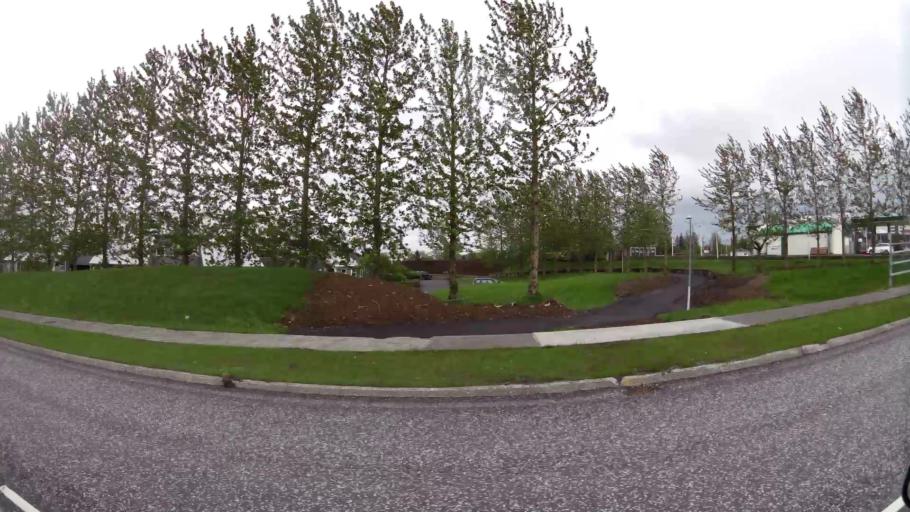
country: IS
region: Capital Region
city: Gardabaer
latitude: 64.0916
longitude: -21.9294
